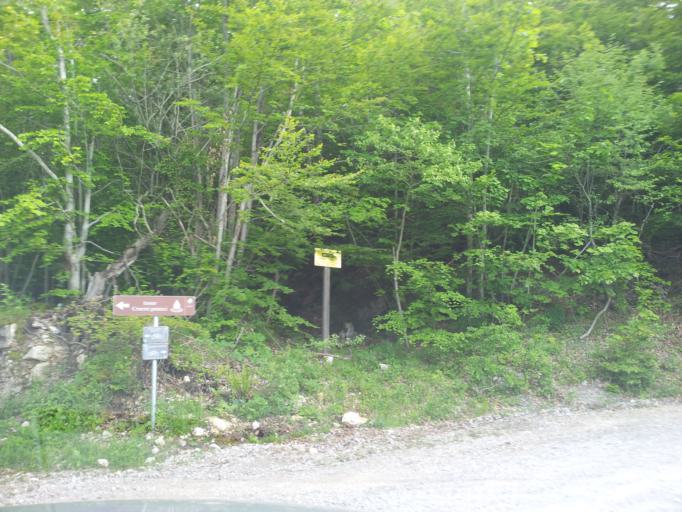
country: HR
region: Zadarska
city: Obrovac
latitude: 44.2961
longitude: 15.6678
